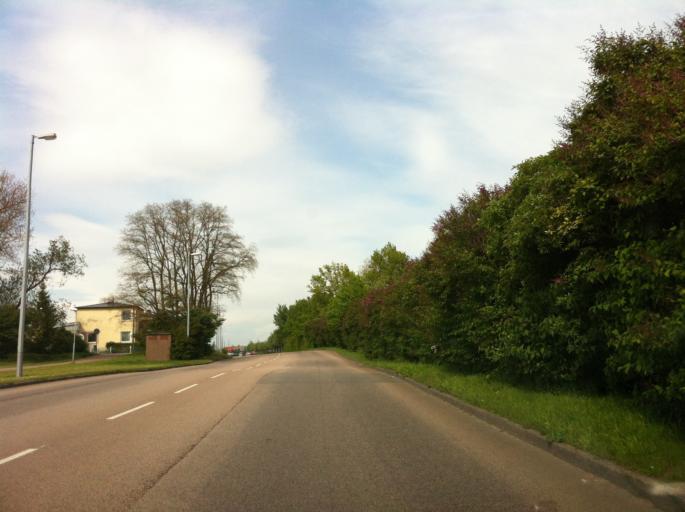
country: SE
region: Skane
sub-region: Landskrona
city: Landskrona
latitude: 55.8740
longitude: 12.8510
